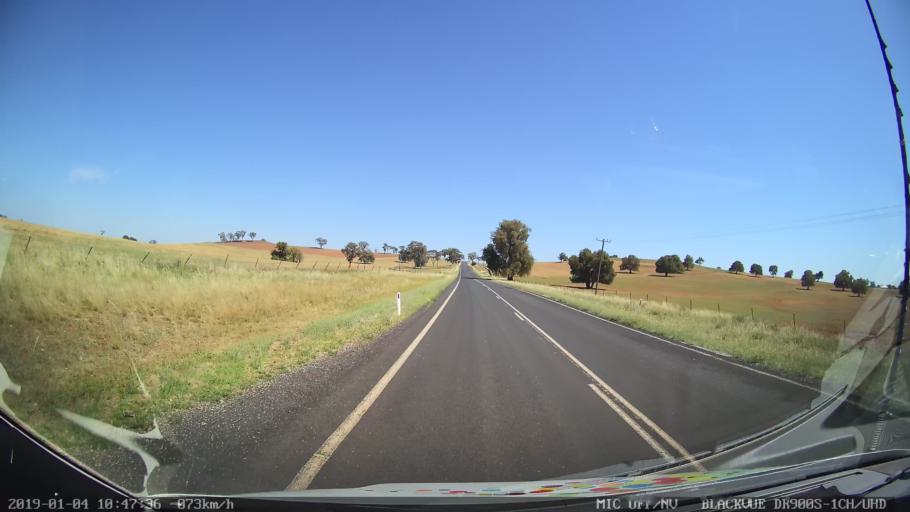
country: AU
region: New South Wales
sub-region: Cabonne
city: Molong
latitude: -33.2685
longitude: 148.7188
